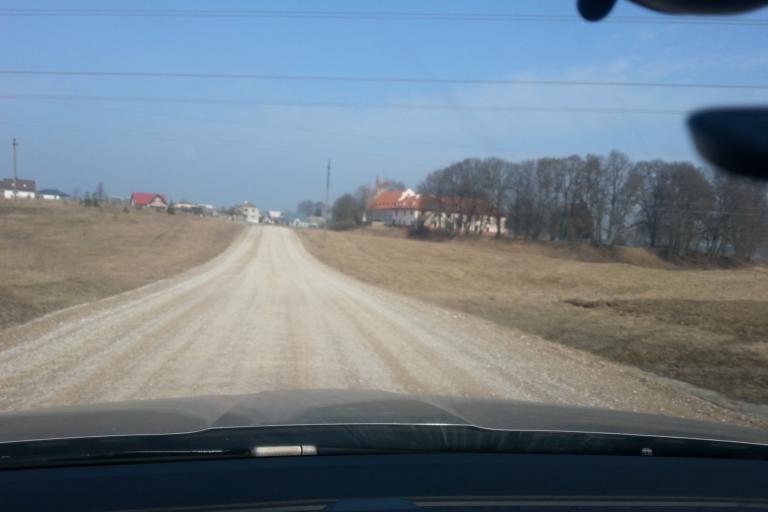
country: LT
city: Trakai
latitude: 54.6031
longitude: 24.9829
